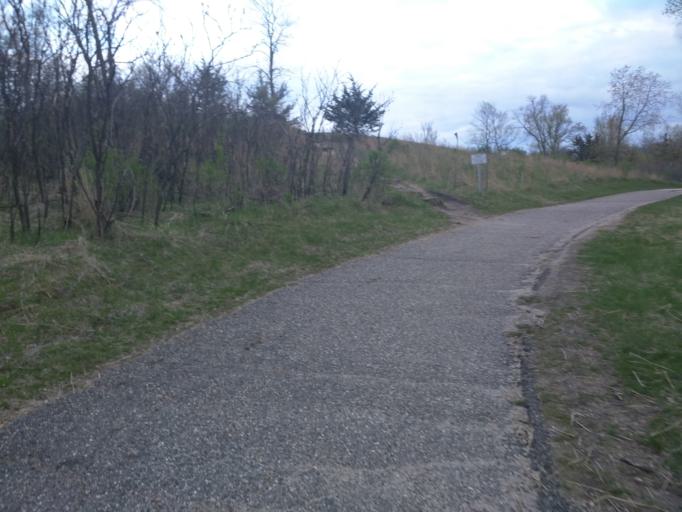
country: US
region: Minnesota
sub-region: Hennepin County
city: Minnetonka
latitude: 44.9008
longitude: -93.4984
